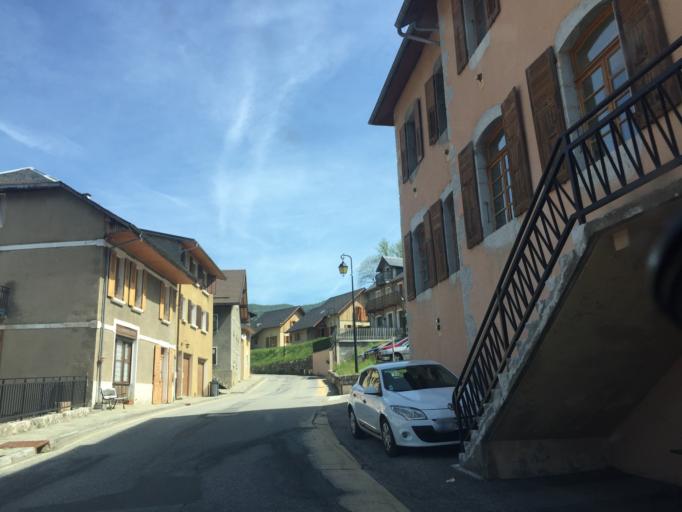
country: FR
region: Rhone-Alpes
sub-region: Departement de l'Isere
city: Barraux
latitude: 45.4525
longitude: 5.8839
